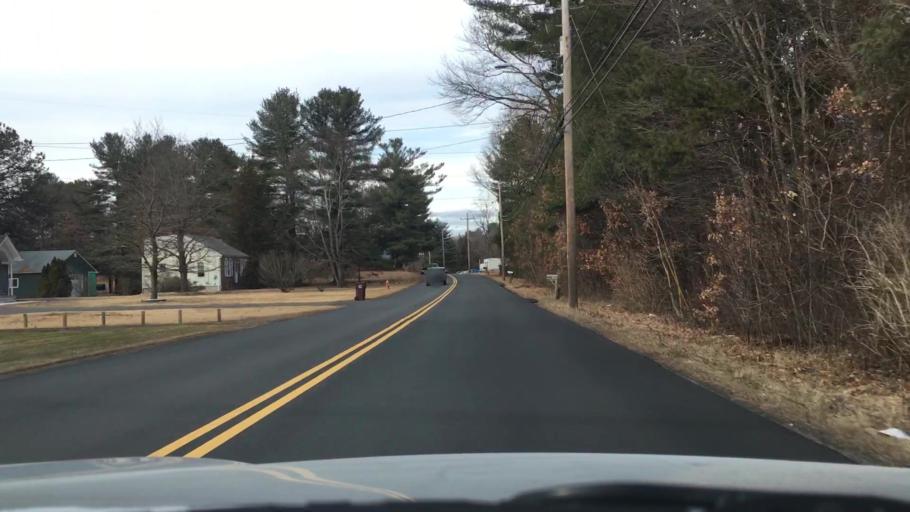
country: US
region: Massachusetts
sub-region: Hampden County
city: Westfield
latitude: 42.1501
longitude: -72.7421
